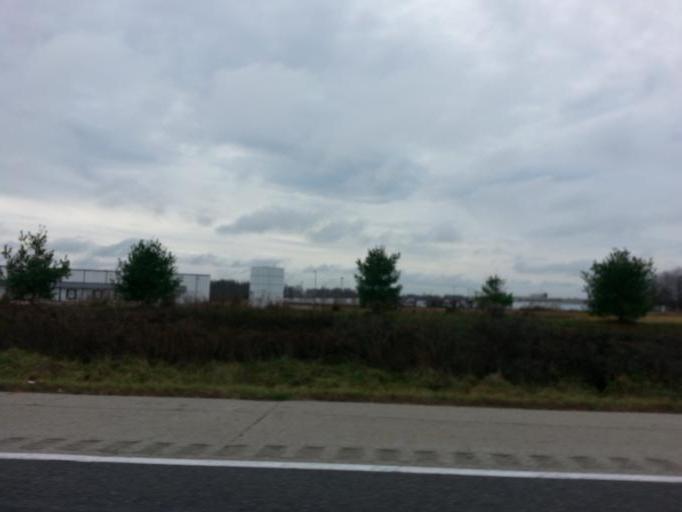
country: US
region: Indiana
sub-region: Ripley County
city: Batesville
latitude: 39.2985
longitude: -85.1878
